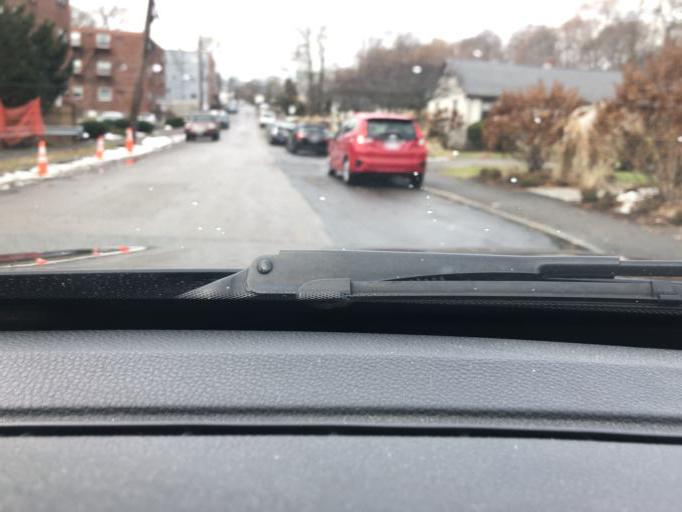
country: US
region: Massachusetts
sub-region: Middlesex County
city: Arlington
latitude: 42.4204
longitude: -71.1641
